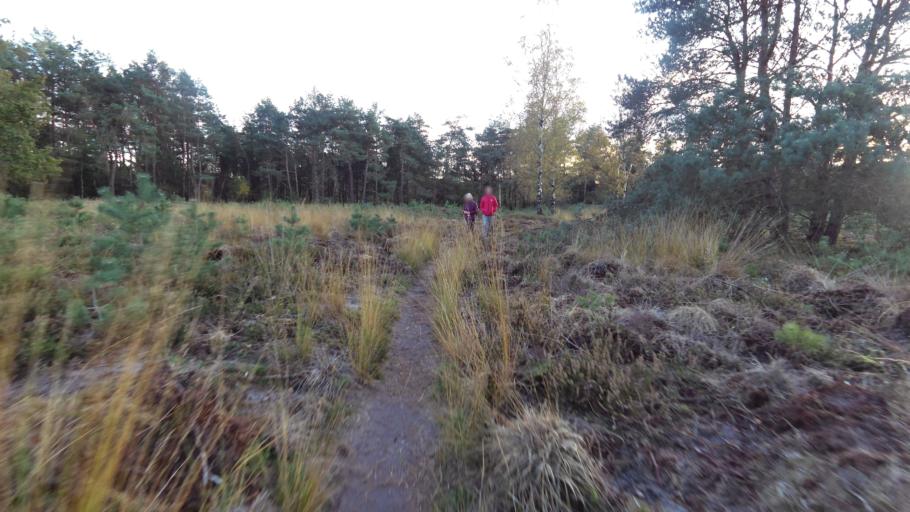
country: NL
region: Gelderland
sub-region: Gemeente Apeldoorn
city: Uddel
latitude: 52.2756
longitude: 5.8115
